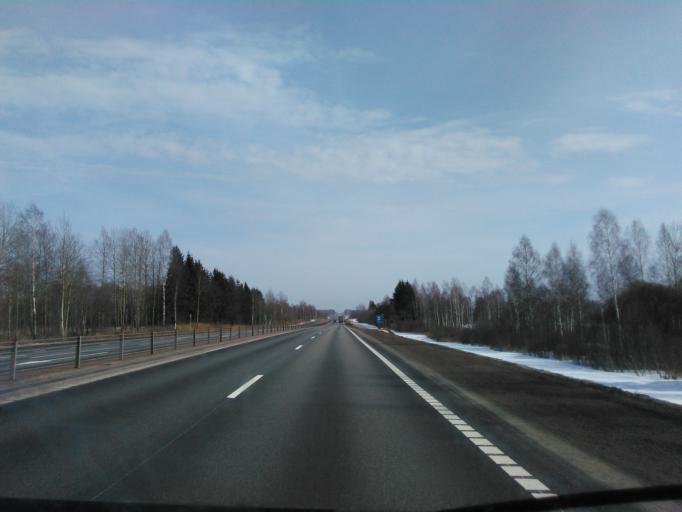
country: BY
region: Vitebsk
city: Dubrowna
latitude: 54.6898
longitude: 30.9209
